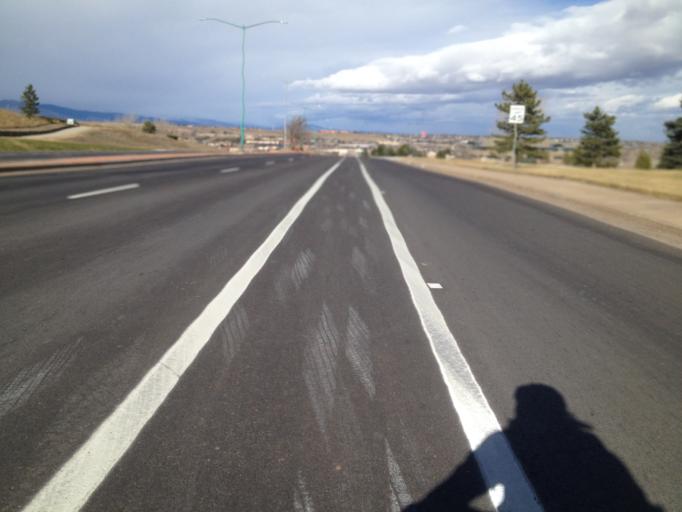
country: US
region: Colorado
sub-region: Boulder County
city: Superior
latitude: 39.9456
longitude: -105.1637
